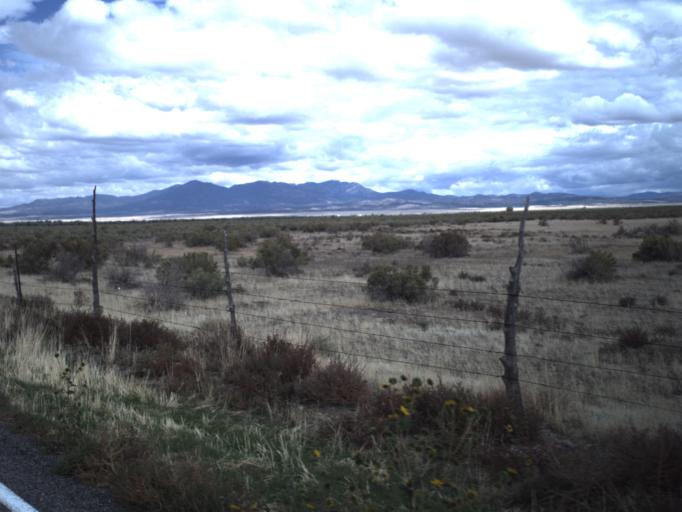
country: US
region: Utah
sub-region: Millard County
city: Fillmore
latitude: 39.0726
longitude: -112.4098
